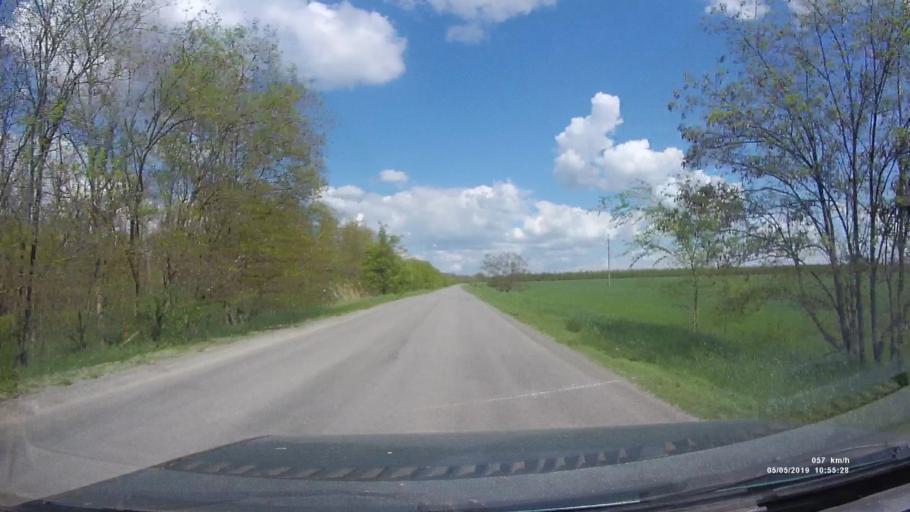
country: RU
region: Rostov
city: Ust'-Donetskiy
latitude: 47.6658
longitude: 40.8211
